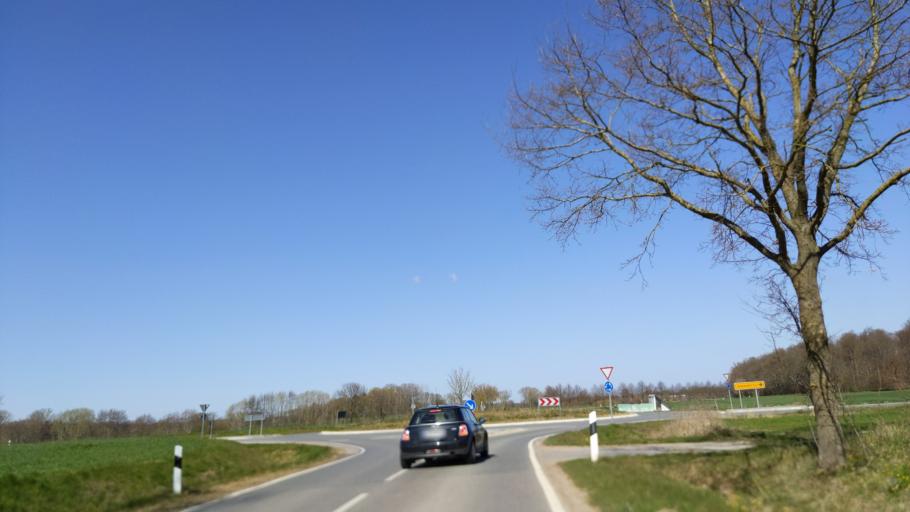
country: DE
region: Schleswig-Holstein
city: Susel
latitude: 54.0143
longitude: 10.6572
